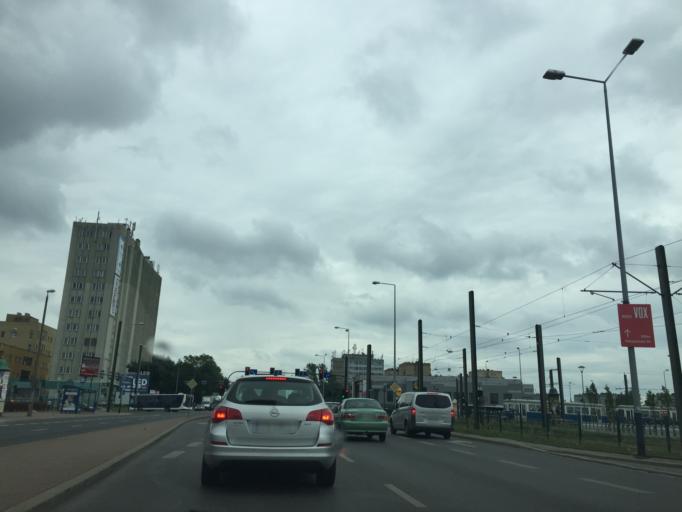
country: PL
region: Lesser Poland Voivodeship
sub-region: Krakow
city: Krakow
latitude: 50.0302
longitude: 19.9370
